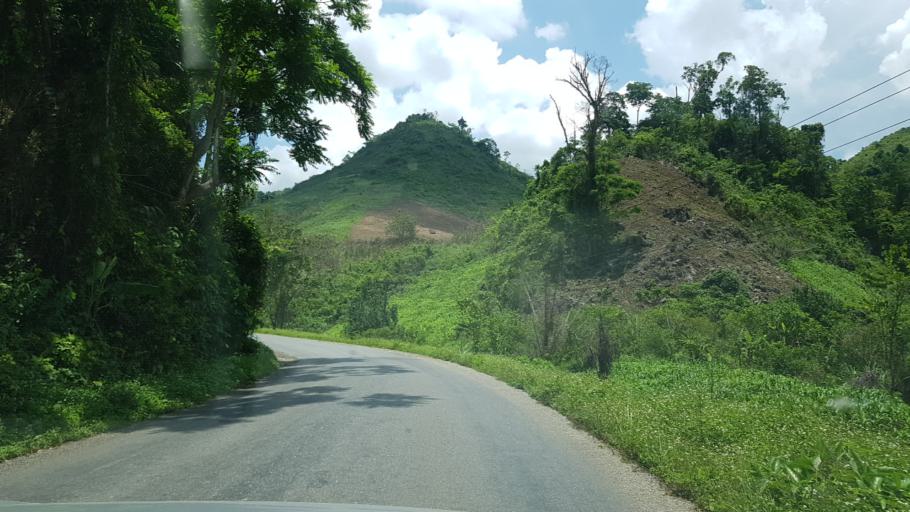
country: LA
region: Vientiane
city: Muang Kasi
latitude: 19.1373
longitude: 102.2900
